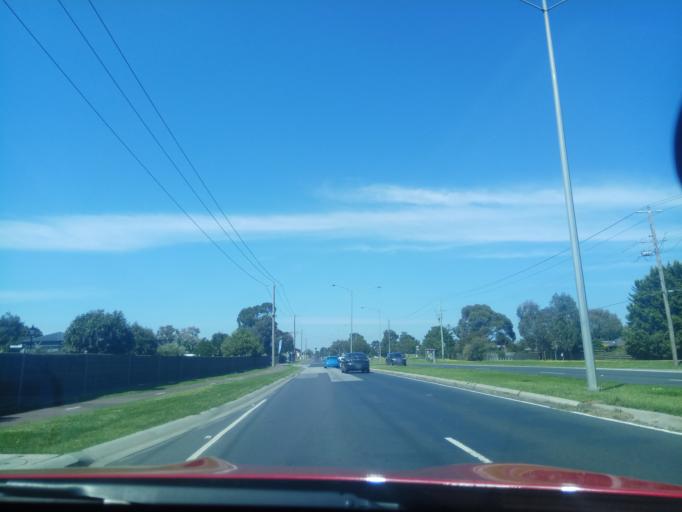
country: AU
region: Victoria
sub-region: Kingston
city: Chelsea Heights
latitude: -38.0306
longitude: 145.1326
